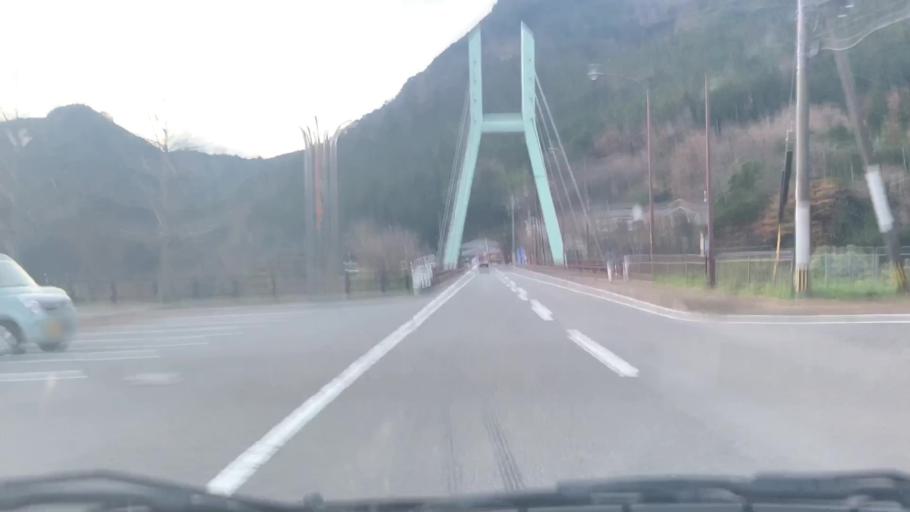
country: JP
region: Nagasaki
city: Omura
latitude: 32.9818
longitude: 130.0263
